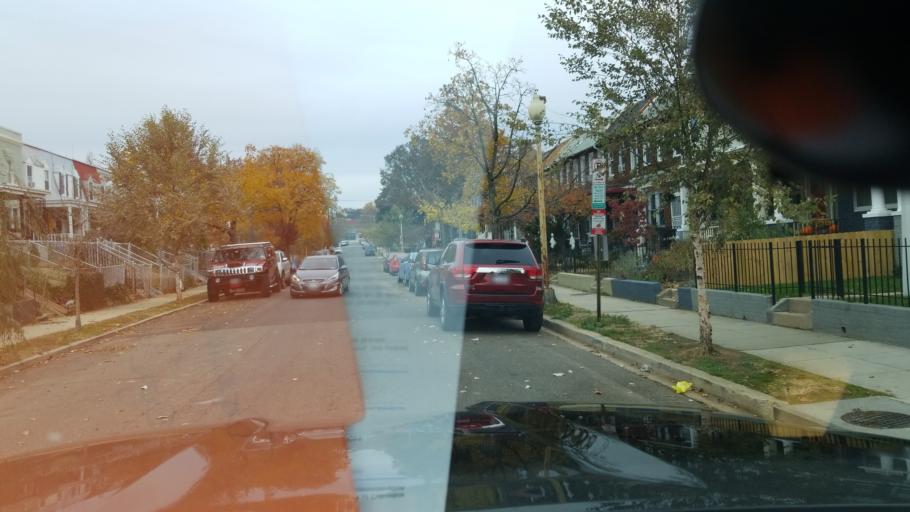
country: US
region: Maryland
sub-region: Prince George's County
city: Mount Rainier
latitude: 38.9218
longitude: -77.0018
